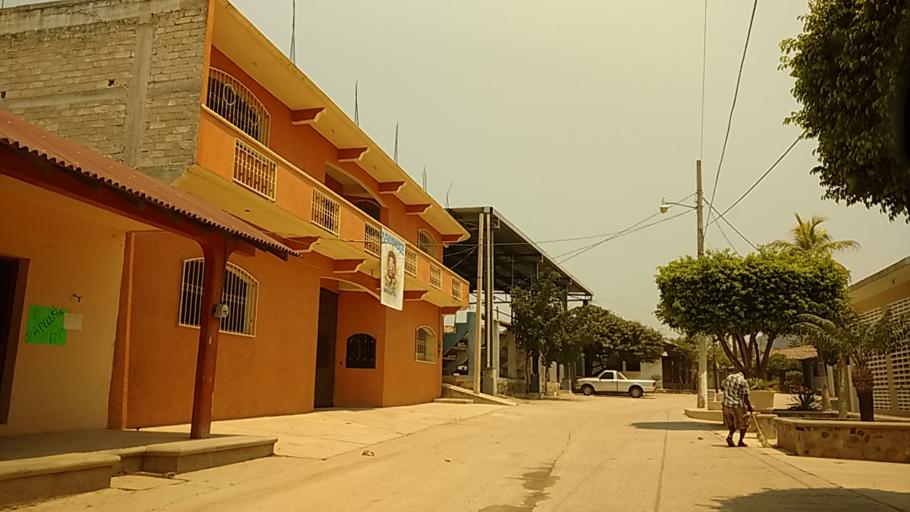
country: MX
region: Guerrero
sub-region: Tecpan de Galeana
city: Villa Rotaria
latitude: 17.2668
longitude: -100.8916
